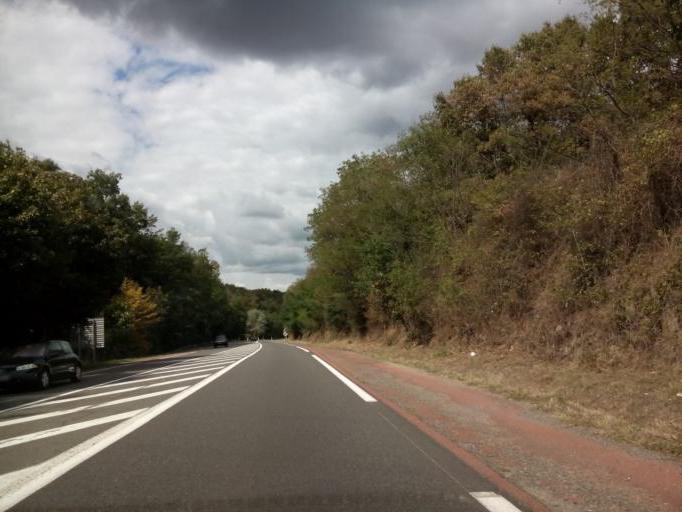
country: FR
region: Rhone-Alpes
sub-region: Departement du Rhone
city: Lissieu
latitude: 45.8455
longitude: 4.7221
